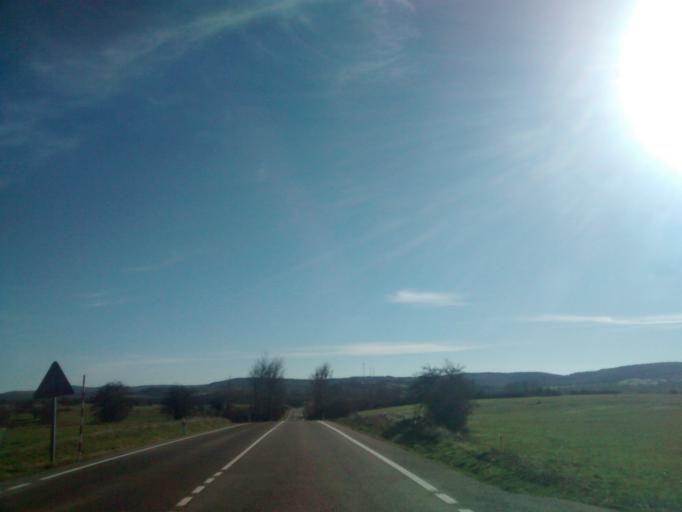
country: ES
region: Cantabria
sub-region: Provincia de Cantabria
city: San Pedro del Romeral
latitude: 42.9773
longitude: -3.8015
